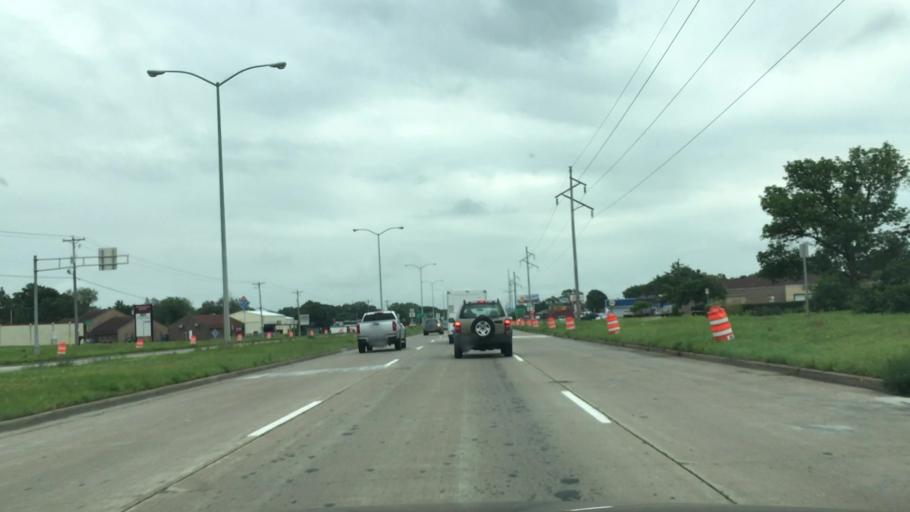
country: US
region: Wisconsin
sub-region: Eau Claire County
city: Eau Claire
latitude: 44.8179
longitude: -91.5421
